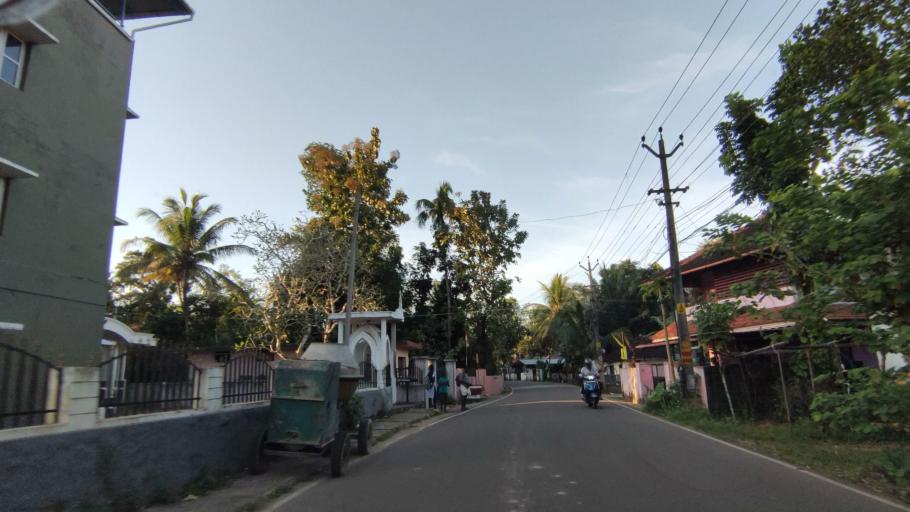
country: IN
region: Kerala
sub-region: Kottayam
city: Kottayam
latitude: 9.6174
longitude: 76.4939
